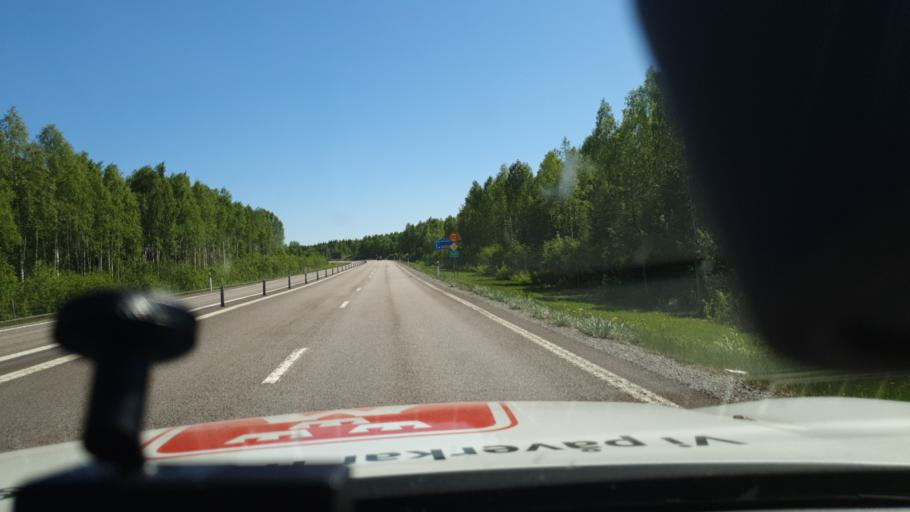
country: SE
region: Norrbotten
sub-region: Kalix Kommun
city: Rolfs
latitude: 65.8872
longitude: 22.9216
